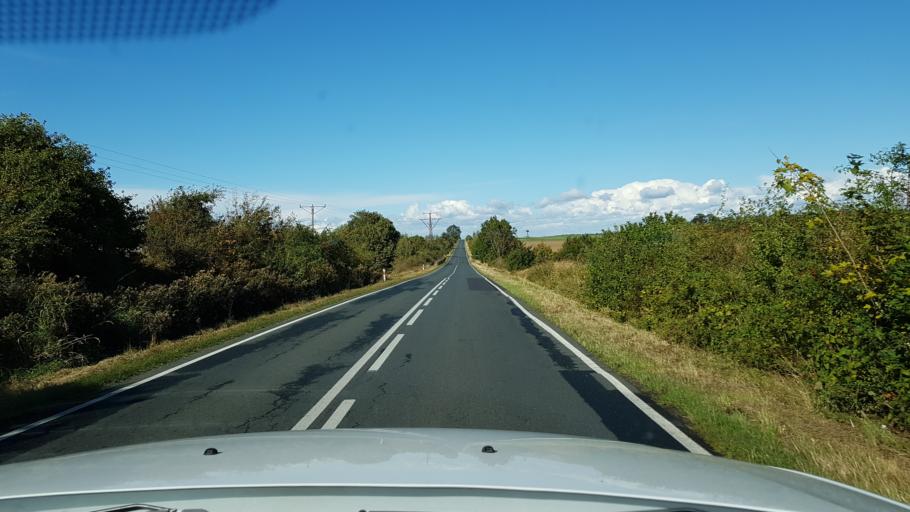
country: PL
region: West Pomeranian Voivodeship
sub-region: Powiat gryfinski
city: Banie
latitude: 53.1367
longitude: 14.6111
